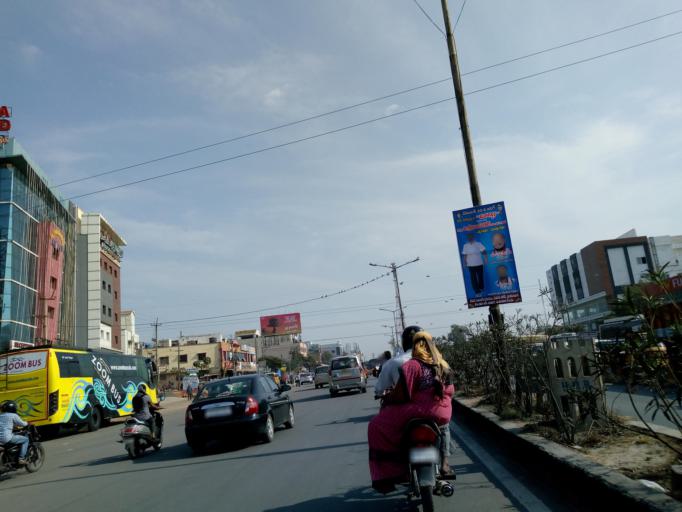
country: IN
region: Telangana
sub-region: Rangareddi
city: Lal Bahadur Nagar
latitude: 17.3448
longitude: 78.5536
